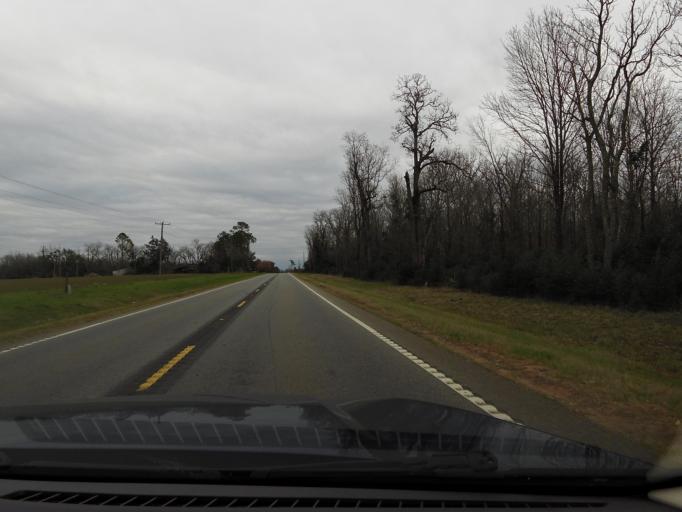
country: US
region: Georgia
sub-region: Randolph County
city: Shellman
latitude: 31.7724
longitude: -84.6410
